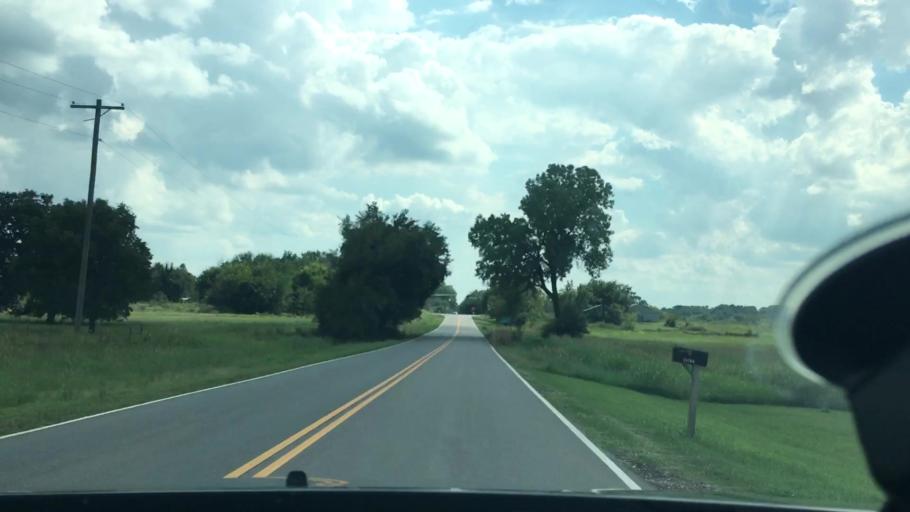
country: US
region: Oklahoma
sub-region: Pottawatomie County
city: Shawnee
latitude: 35.3362
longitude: -96.8072
